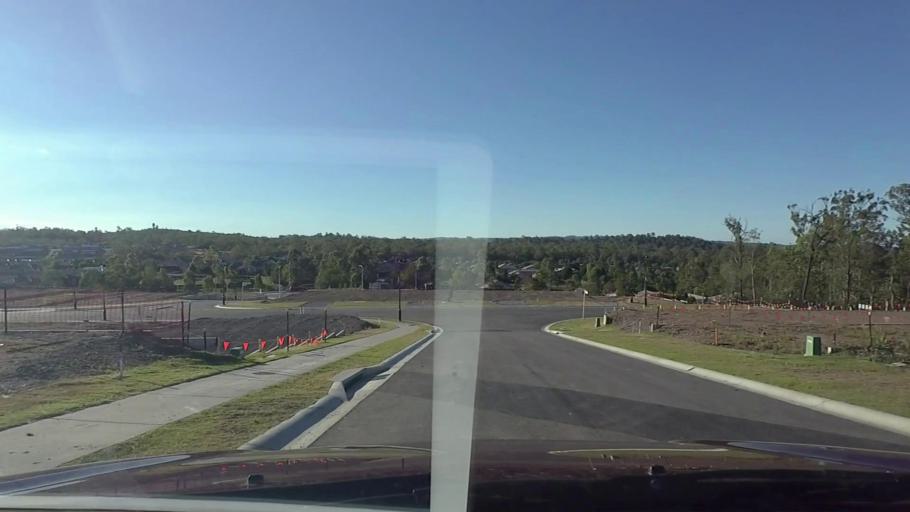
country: AU
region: Queensland
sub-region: Logan
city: Windaroo
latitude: -27.7239
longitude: 153.1696
